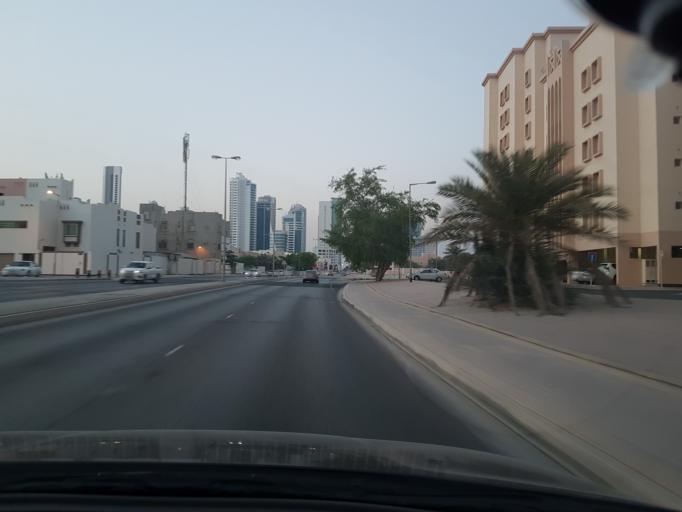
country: BH
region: Manama
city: Jidd Hafs
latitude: 26.2234
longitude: 50.5518
